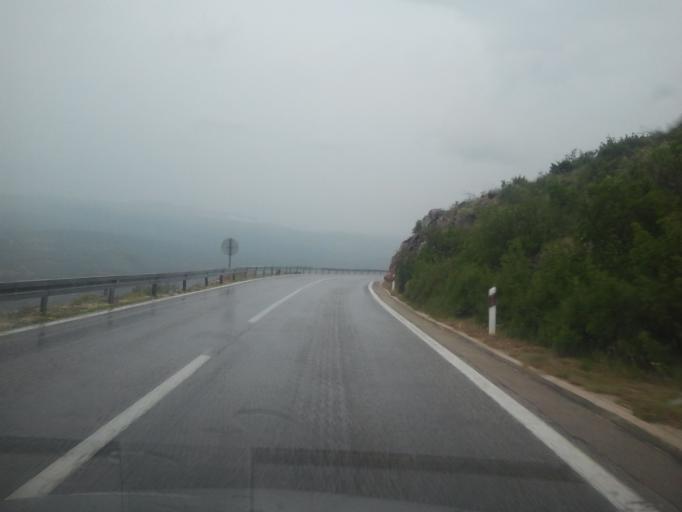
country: HR
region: Zadarska
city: Obrovac
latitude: 44.2256
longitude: 15.7760
